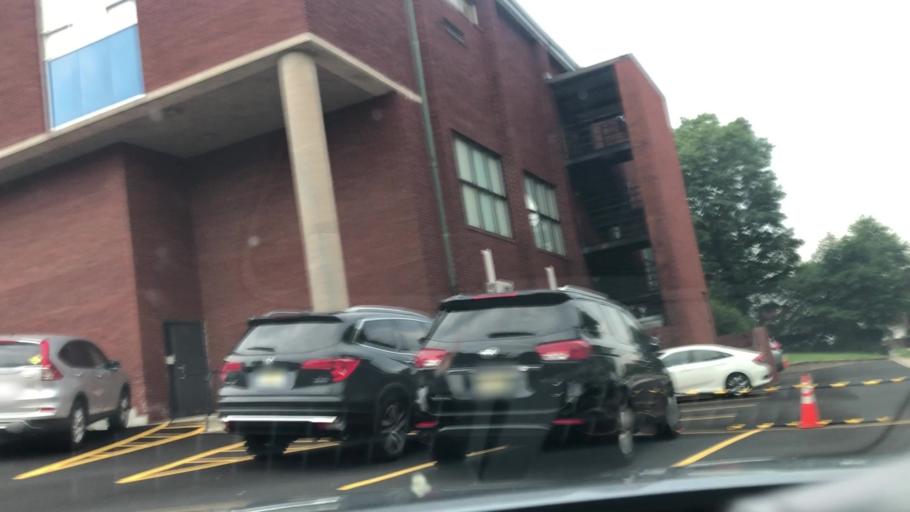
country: US
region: New Jersey
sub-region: Bergen County
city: Fort Lee
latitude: 40.8473
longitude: -73.9796
